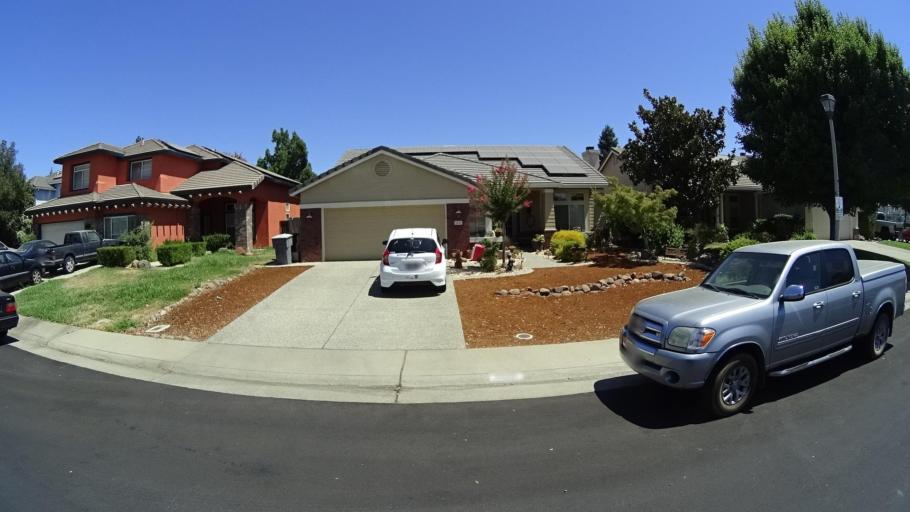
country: US
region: California
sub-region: Placer County
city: Rocklin
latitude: 38.8180
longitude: -121.2712
